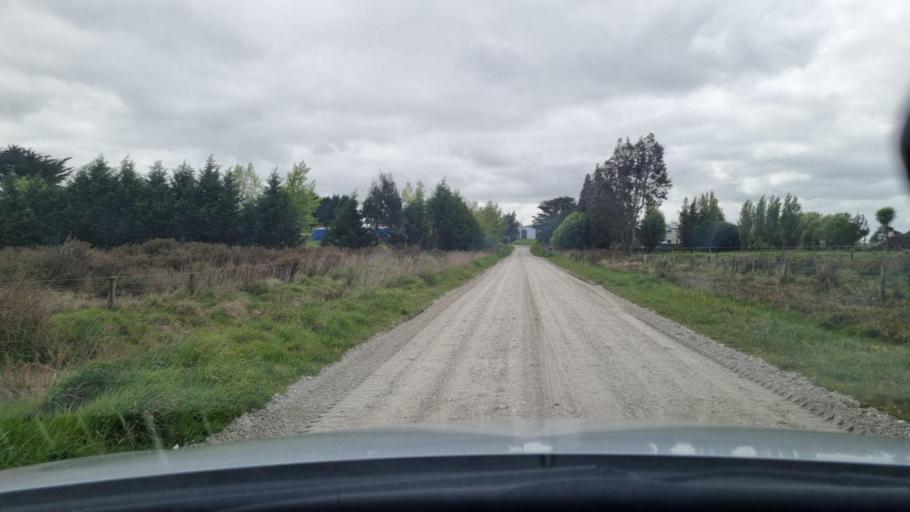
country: NZ
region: Southland
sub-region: Invercargill City
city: Invercargill
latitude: -46.4344
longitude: 168.3896
